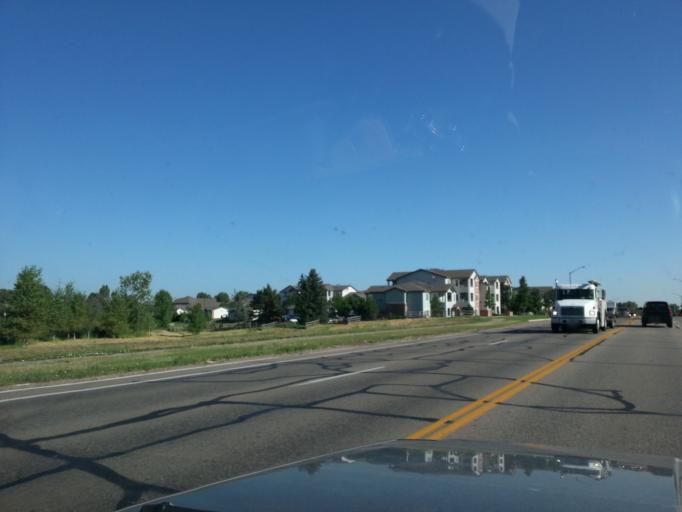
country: US
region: Colorado
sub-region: Larimer County
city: Fort Collins
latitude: 40.5277
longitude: -105.0393
